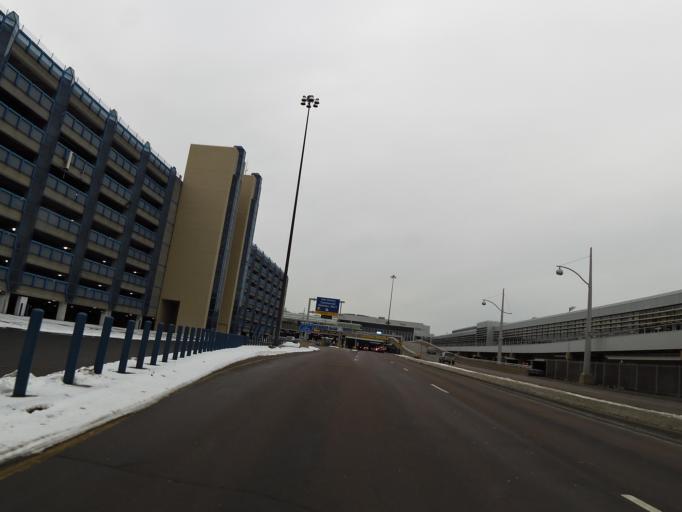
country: US
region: Minnesota
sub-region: Dakota County
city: Mendota Heights
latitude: 44.8831
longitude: -93.2076
